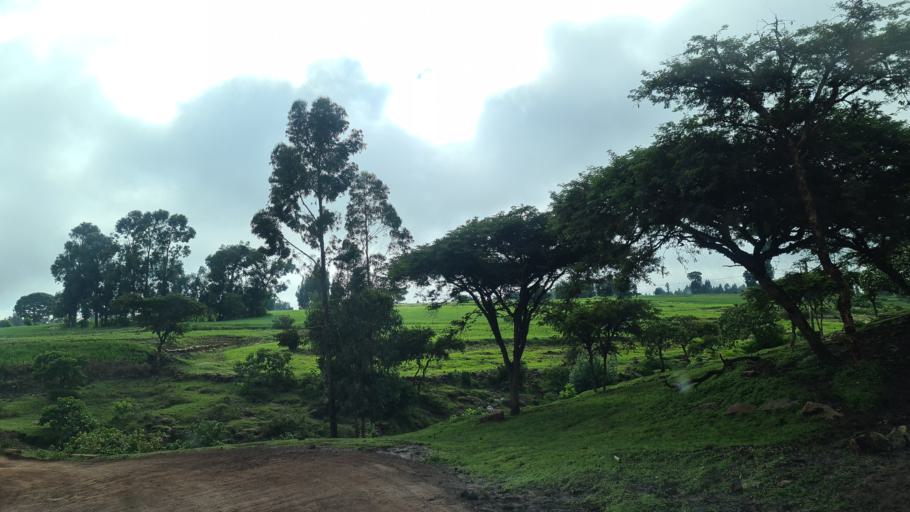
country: ET
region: Oromiya
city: Huruta
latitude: 8.1249
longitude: 39.3748
